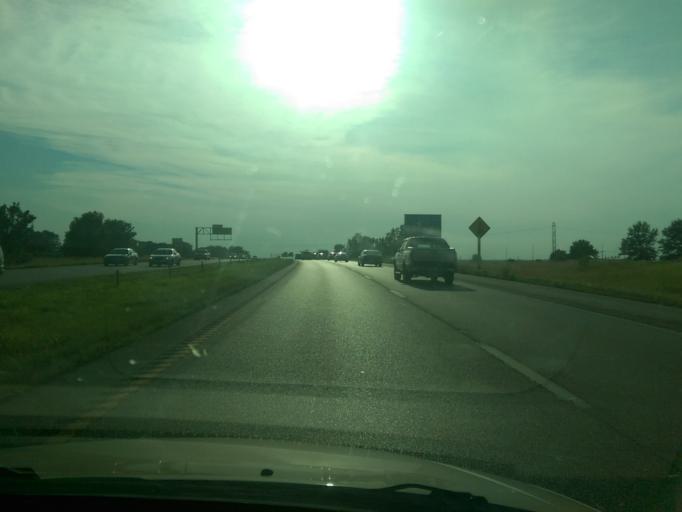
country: US
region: Missouri
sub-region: Clay County
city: Gladstone
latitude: 39.1795
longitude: -94.5729
